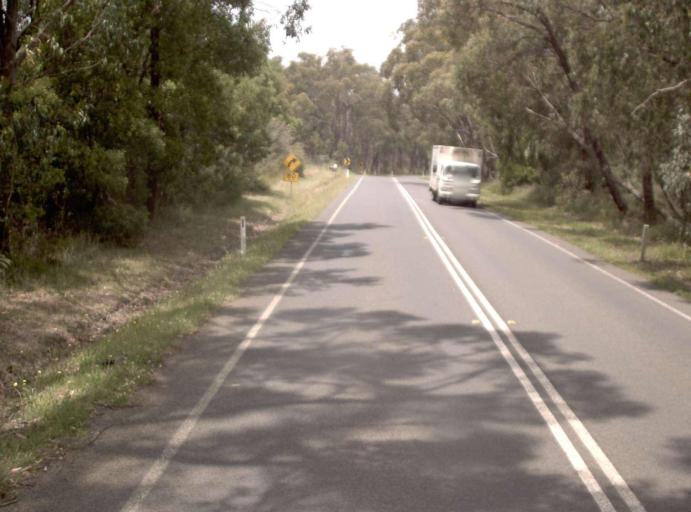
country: AU
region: Victoria
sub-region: Latrobe
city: Traralgon
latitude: -38.4052
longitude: 146.7509
